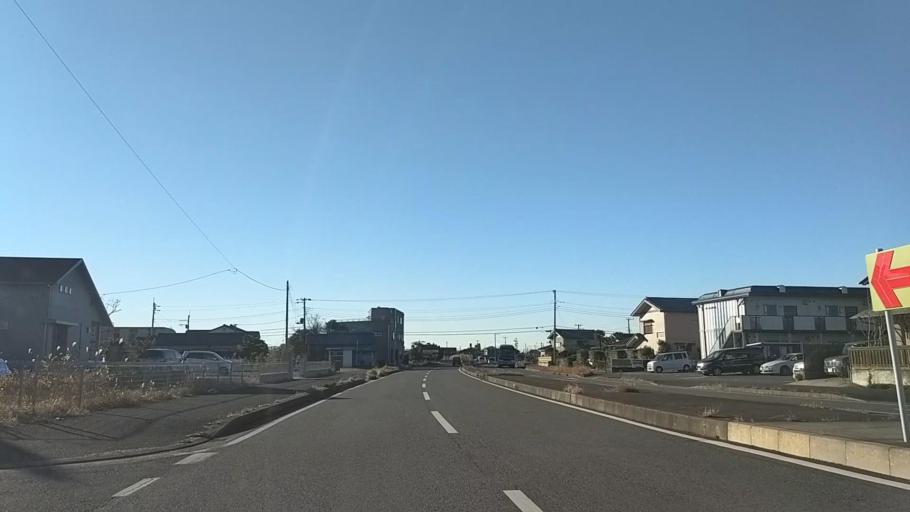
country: JP
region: Chiba
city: Kisarazu
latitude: 35.3987
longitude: 139.9211
